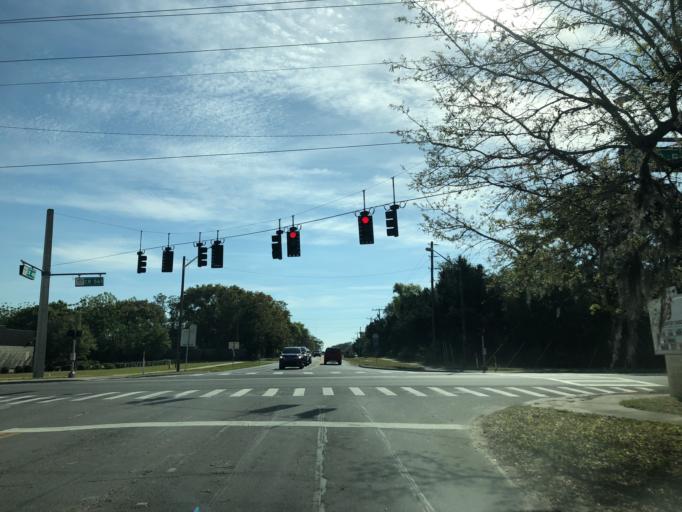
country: US
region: Florida
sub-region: Lake County
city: Astatula
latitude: 28.7100
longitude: -81.7335
